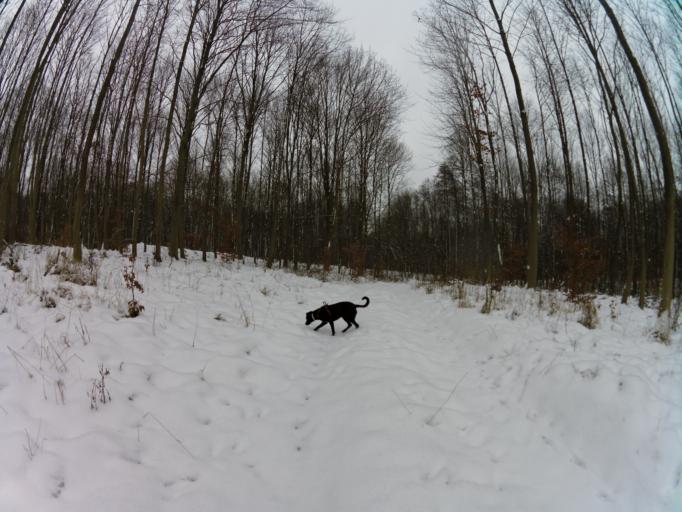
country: PL
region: West Pomeranian Voivodeship
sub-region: Powiat choszczenski
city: Recz
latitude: 53.3286
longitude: 15.5450
